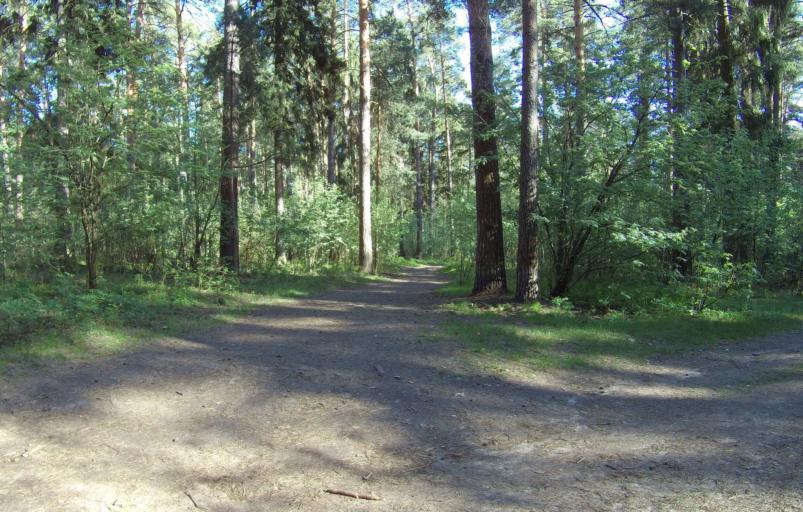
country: RU
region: Moskovskaya
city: Kratovo
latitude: 55.5634
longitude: 38.1851
